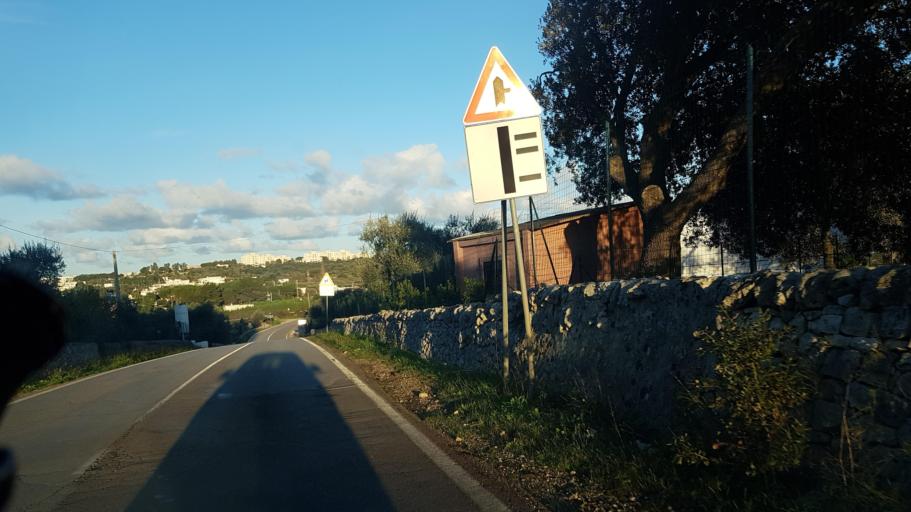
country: IT
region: Apulia
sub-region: Provincia di Brindisi
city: Ostuni
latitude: 40.7146
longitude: 17.5585
